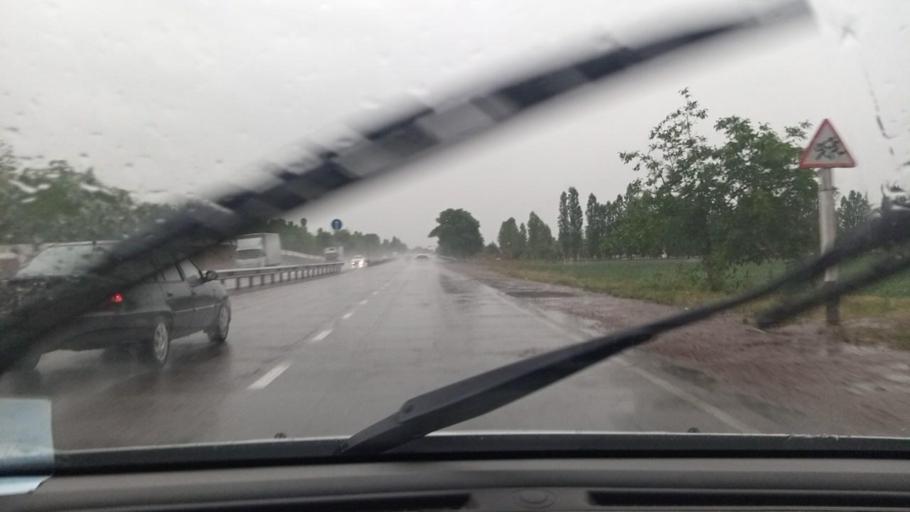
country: UZ
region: Toshkent
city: Ohangaron
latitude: 40.8990
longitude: 69.6798
